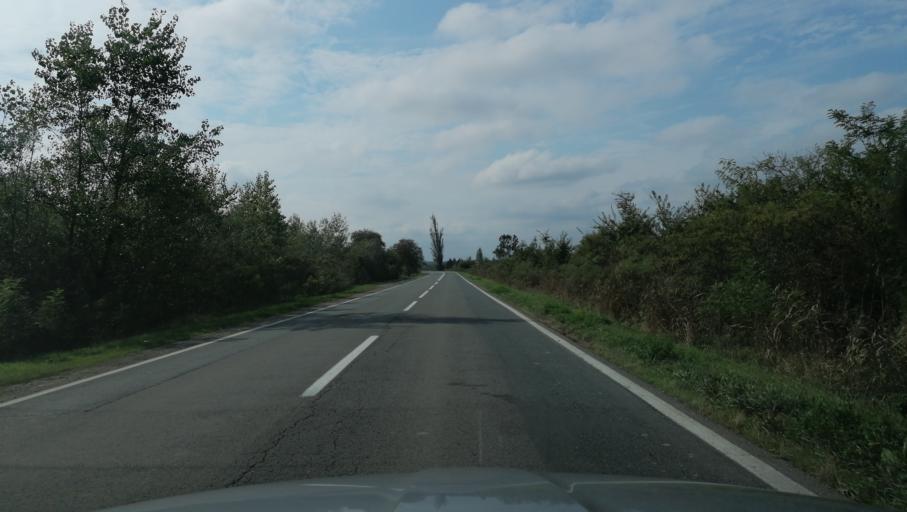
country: RS
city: Bosut
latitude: 44.9225
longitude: 19.3187
